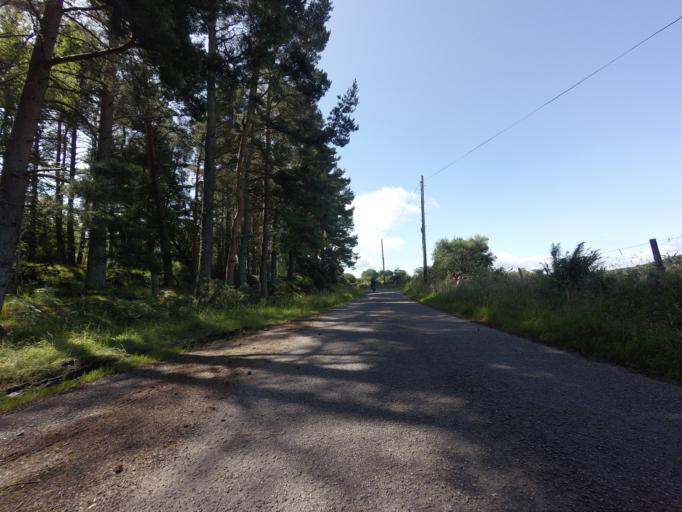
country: GB
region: Scotland
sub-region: Highland
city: Nairn
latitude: 57.5031
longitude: -3.9382
